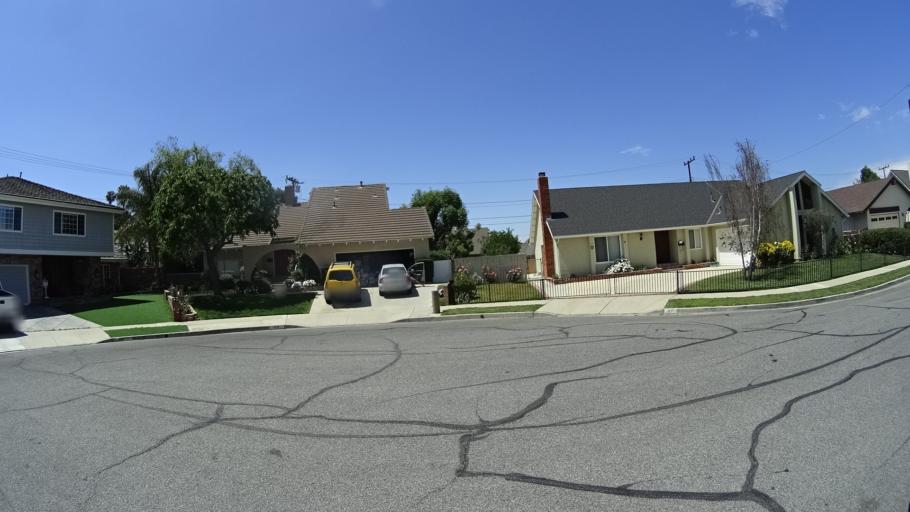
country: US
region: California
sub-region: Ventura County
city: Casa Conejo
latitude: 34.1776
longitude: -118.9167
